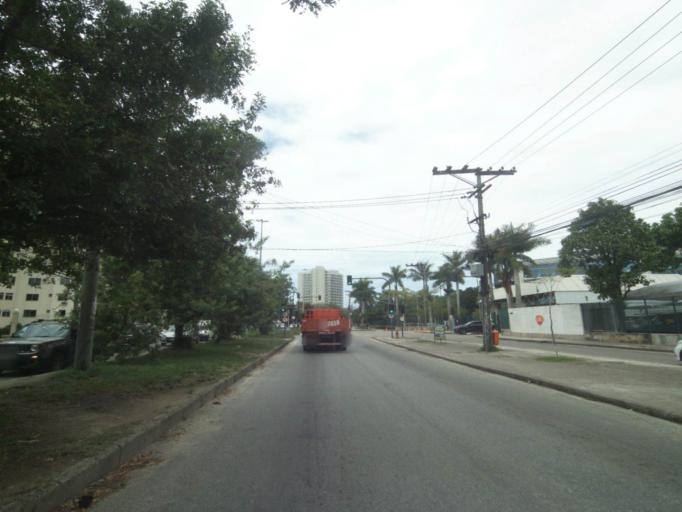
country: BR
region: Rio de Janeiro
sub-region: Nilopolis
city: Nilopolis
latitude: -22.9723
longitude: -43.4140
